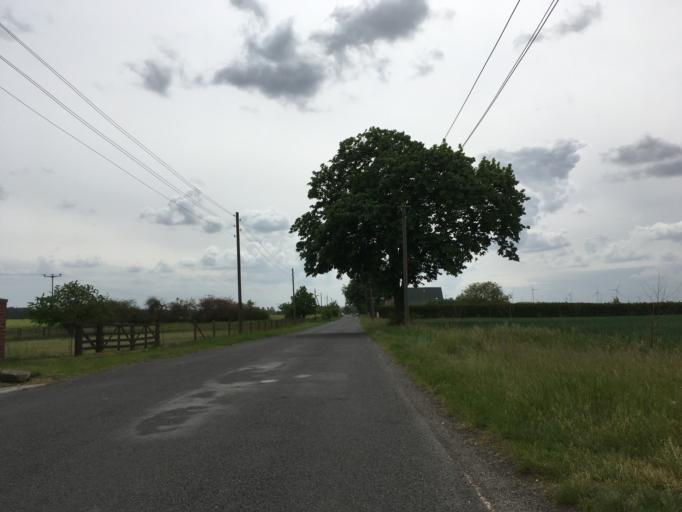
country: DE
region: Brandenburg
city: Melchow
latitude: 52.7239
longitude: 13.7432
